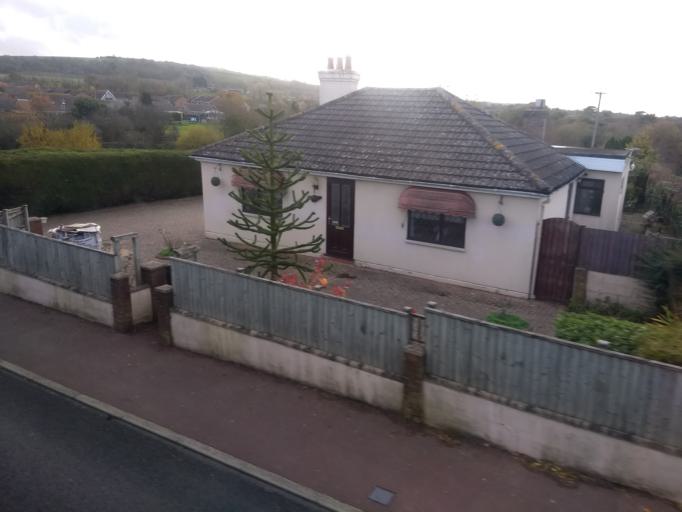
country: GB
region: England
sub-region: Isle of Wight
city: Newport
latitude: 50.7016
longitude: -1.3227
